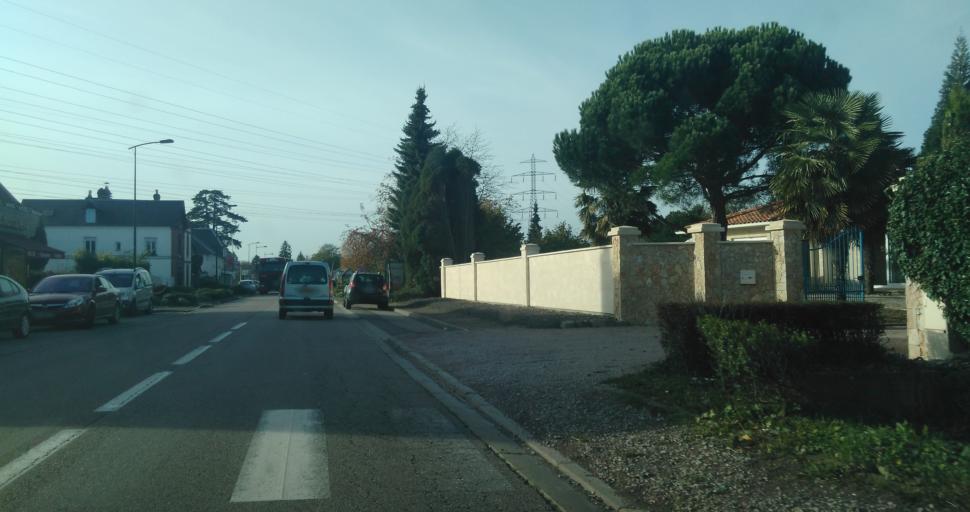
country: FR
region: Haute-Normandie
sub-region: Departement de l'Eure
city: Caumont
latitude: 49.3533
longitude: 0.9127
